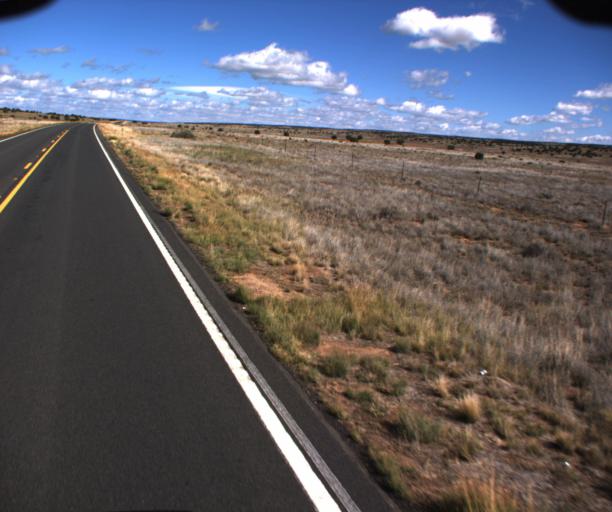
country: US
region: Arizona
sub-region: Apache County
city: Houck
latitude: 34.9306
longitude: -109.2375
